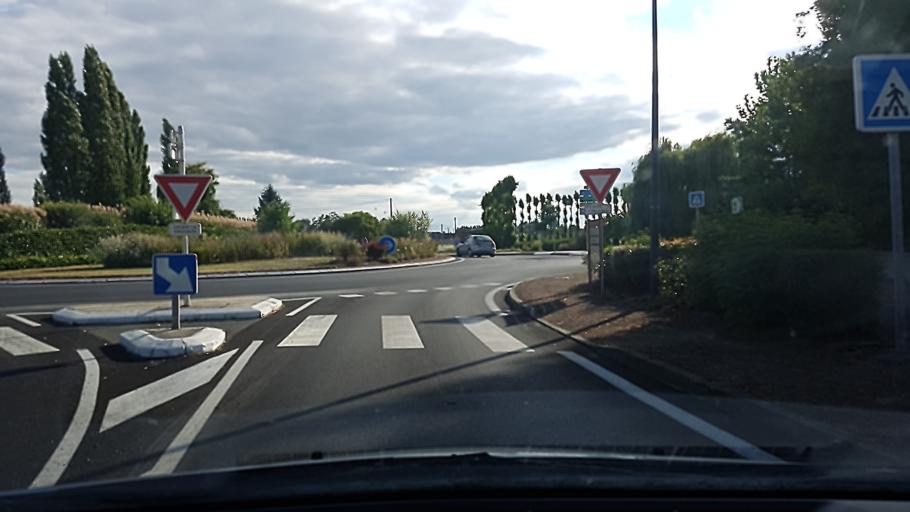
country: FR
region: Pays de la Loire
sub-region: Departement de Maine-et-Loire
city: Maze
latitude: 47.4542
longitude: -0.2756
